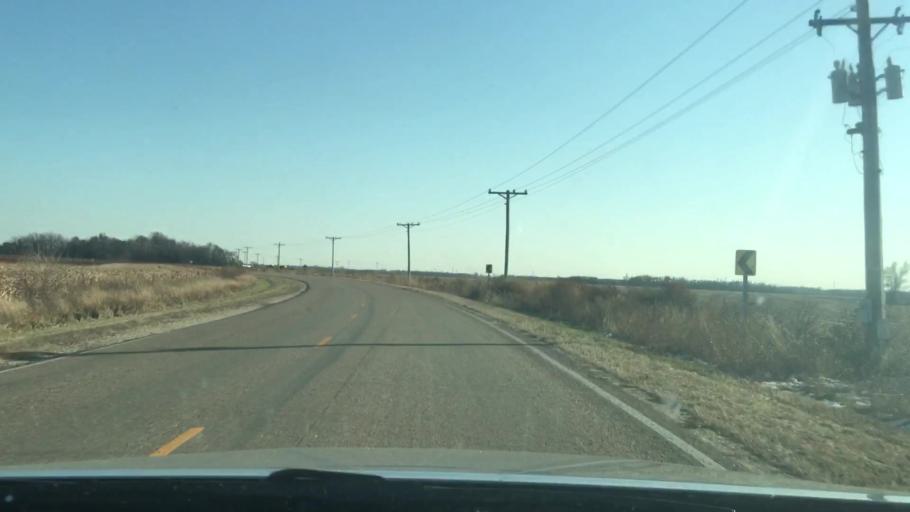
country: US
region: Kansas
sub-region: Reno County
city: Nickerson
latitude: 38.2662
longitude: -98.0911
